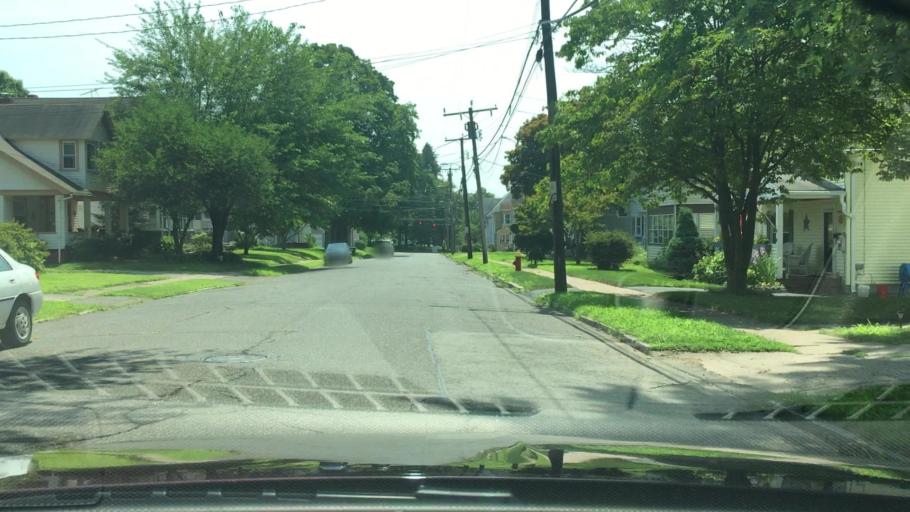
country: US
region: Connecticut
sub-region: Hartford County
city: East Hartford
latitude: 41.7812
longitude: -72.6076
